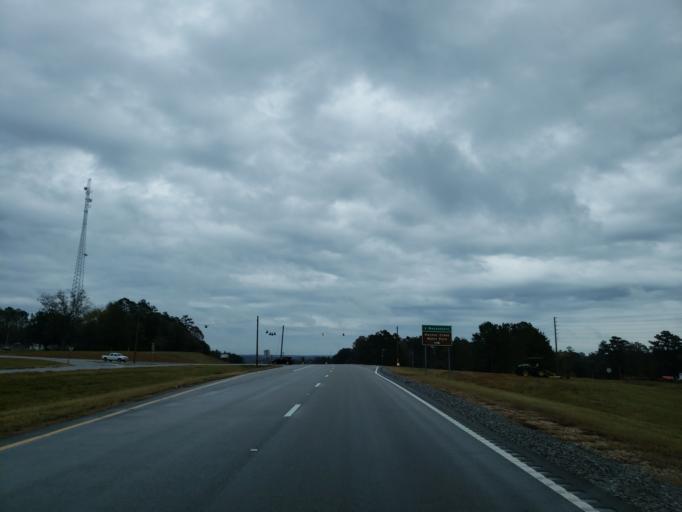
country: US
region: Mississippi
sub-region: Wayne County
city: Waynesboro
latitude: 31.6833
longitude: -88.6945
